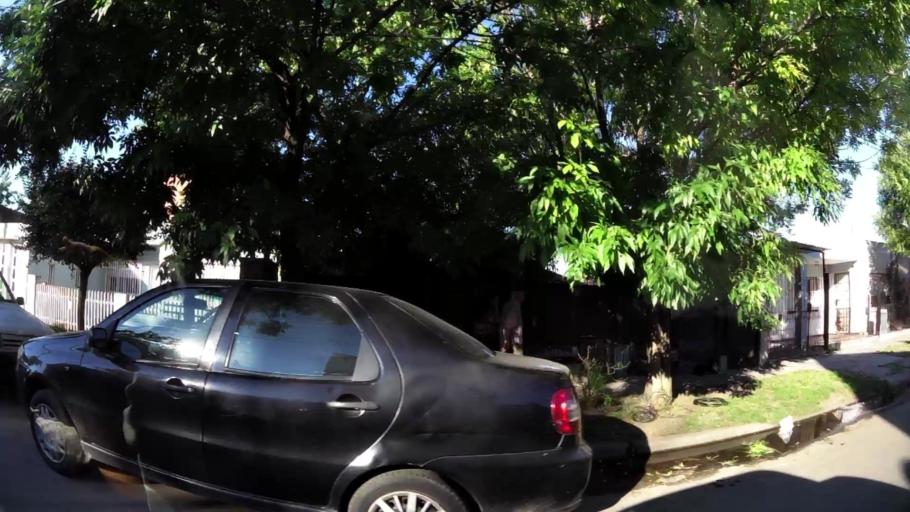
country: AR
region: Buenos Aires
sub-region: Partido de Moron
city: Moron
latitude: -34.6850
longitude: -58.6283
